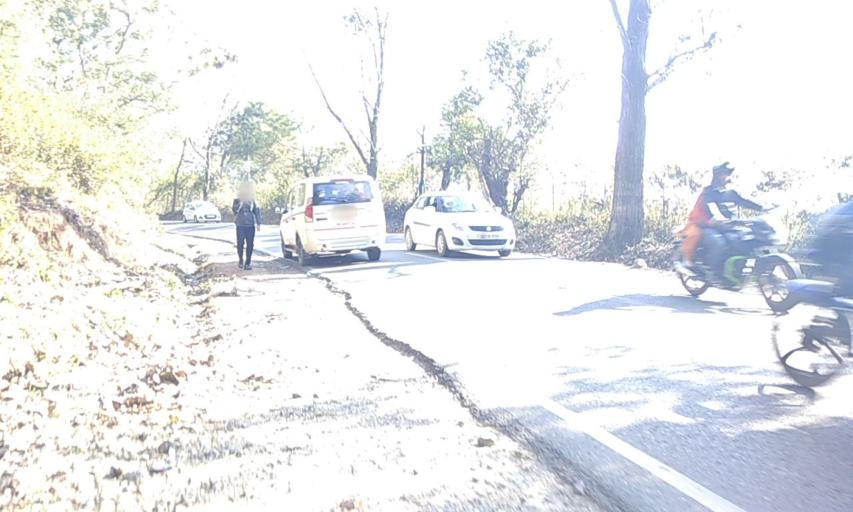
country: IN
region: Himachal Pradesh
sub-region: Kangra
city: Palampur
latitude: 32.1039
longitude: 76.5550
